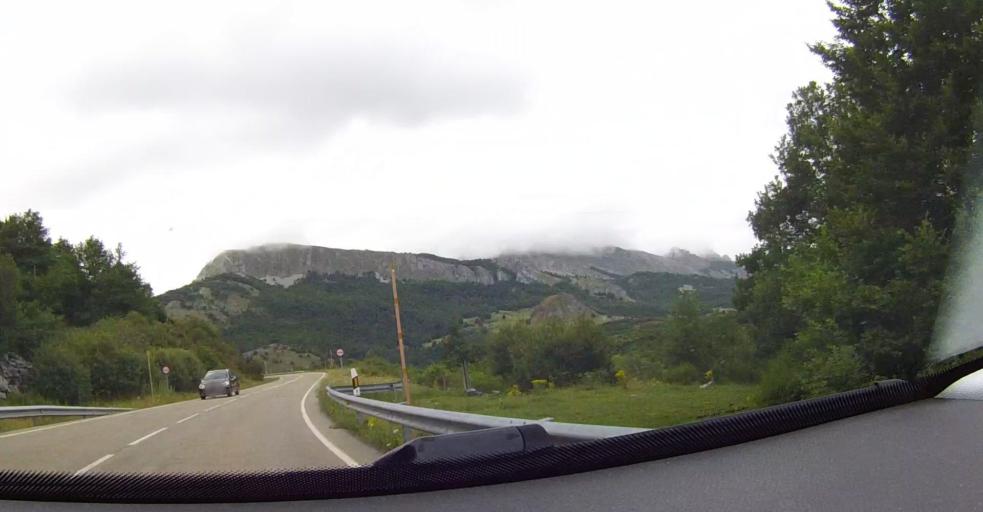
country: ES
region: Castille and Leon
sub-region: Provincia de Leon
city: Buron
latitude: 43.0221
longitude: -5.0360
